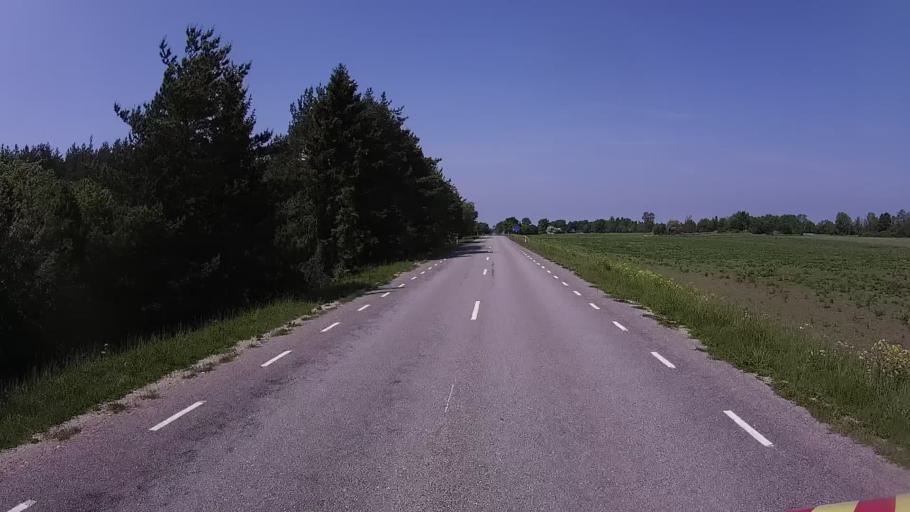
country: EE
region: Saare
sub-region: Kuressaare linn
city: Kuressaare
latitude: 58.3604
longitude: 22.0616
